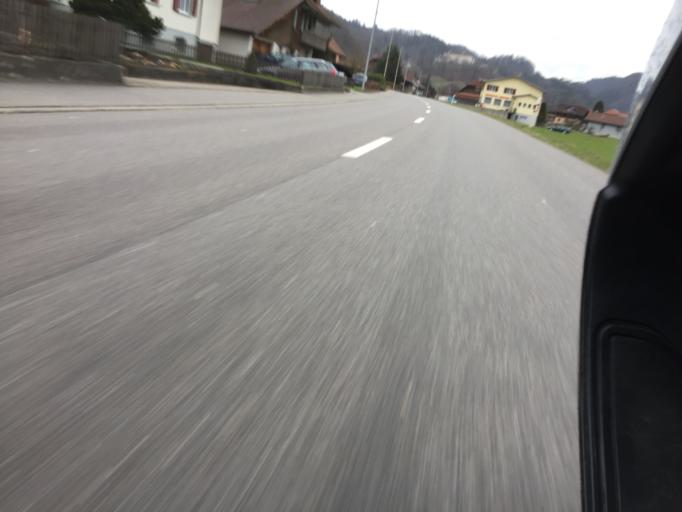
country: CH
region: Bern
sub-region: Emmental District
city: Krauchthal
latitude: 47.0134
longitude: 7.5678
